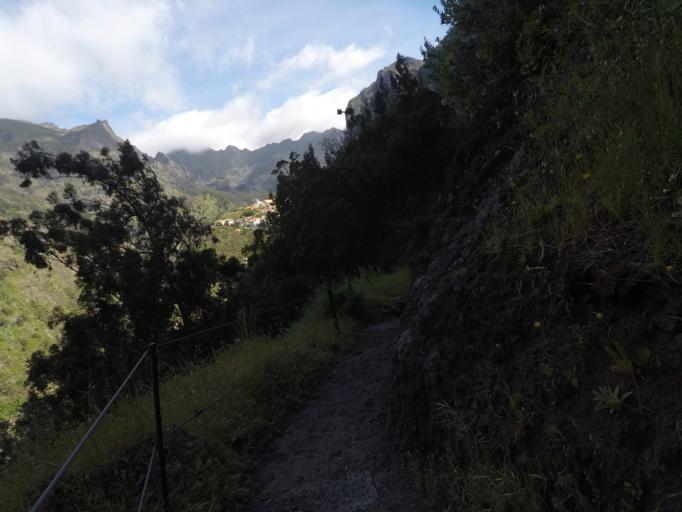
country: PT
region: Madeira
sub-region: Camara de Lobos
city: Curral das Freiras
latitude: 32.7142
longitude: -16.9645
